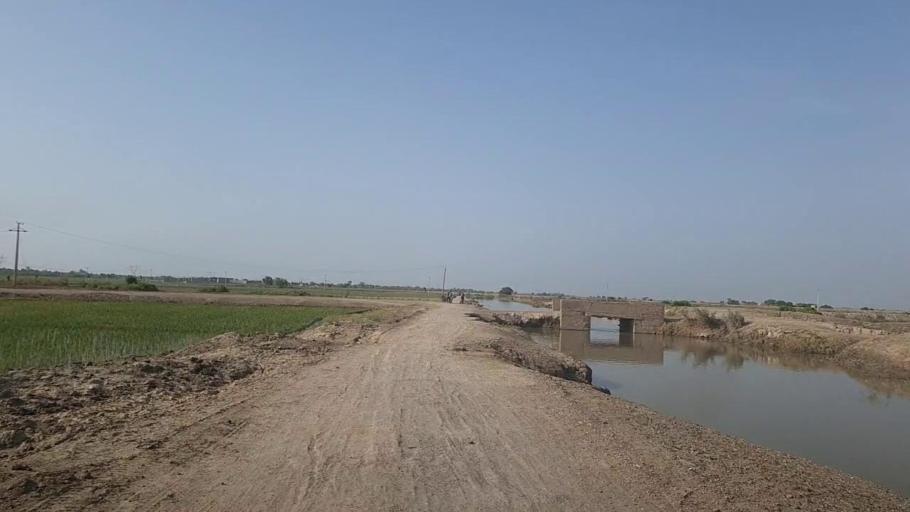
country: PK
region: Sindh
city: Sita Road
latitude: 27.1109
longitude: 67.8766
